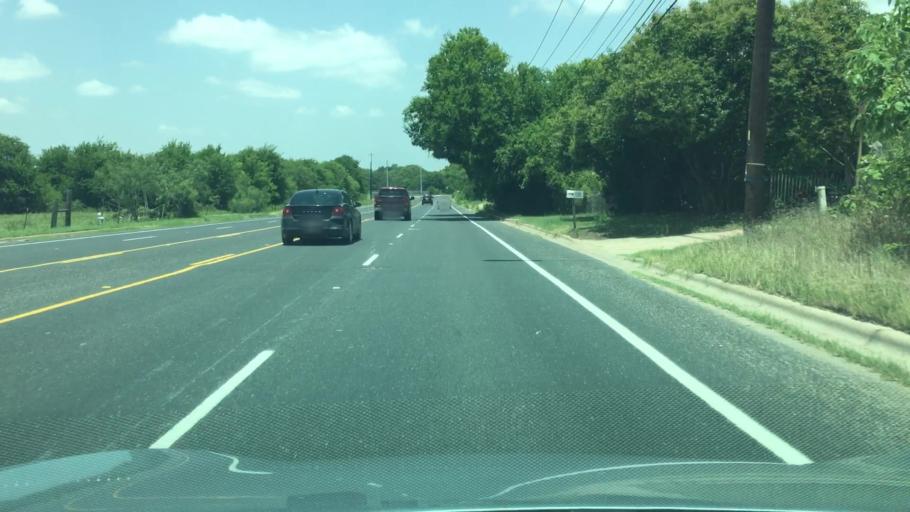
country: US
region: Texas
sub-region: Travis County
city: Austin
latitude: 30.1888
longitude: -97.6949
